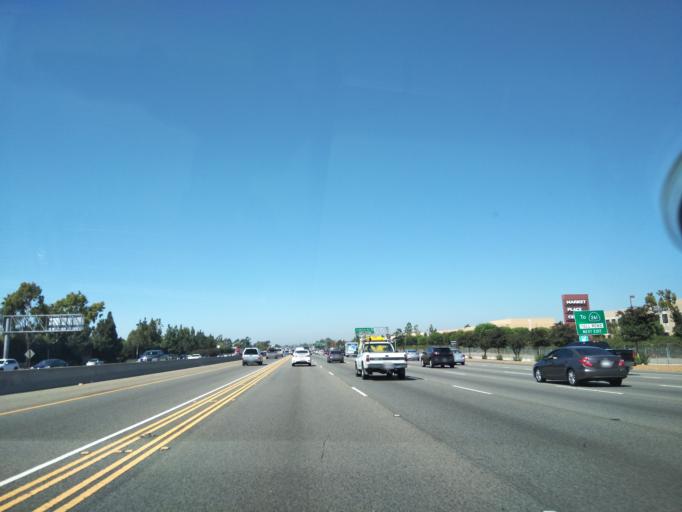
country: US
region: California
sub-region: Orange County
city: Tustin
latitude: 33.7148
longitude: -117.7879
